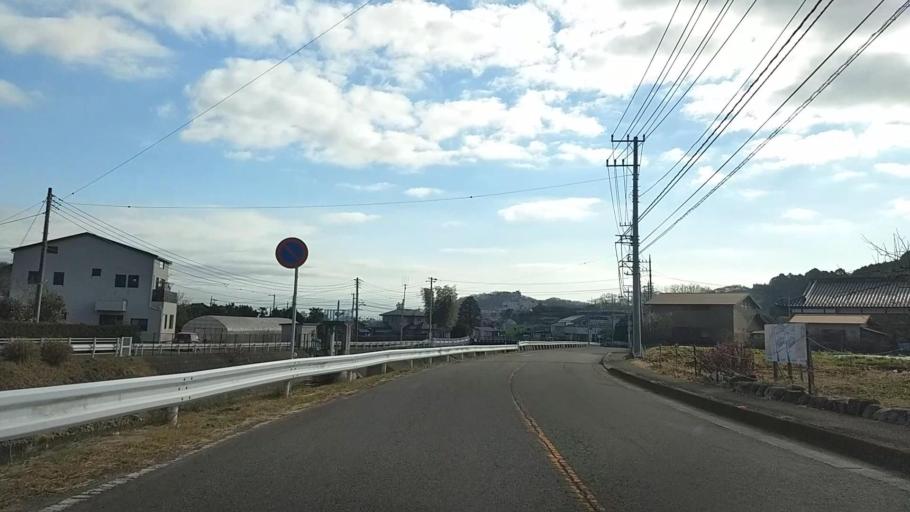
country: JP
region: Kanagawa
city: Isehara
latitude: 35.4366
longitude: 139.3058
